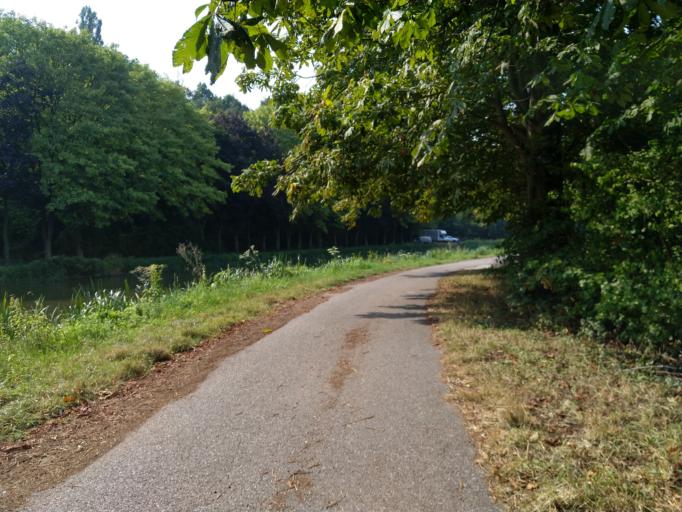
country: BE
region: Wallonia
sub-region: Province du Hainaut
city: Seneffe
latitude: 50.5146
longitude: 4.2716
